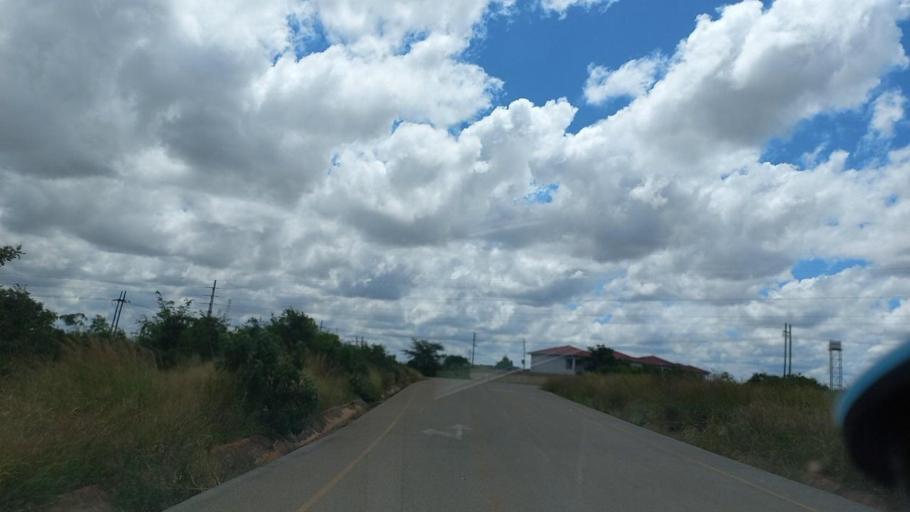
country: ZM
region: Lusaka
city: Lusaka
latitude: -15.4913
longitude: 28.3722
